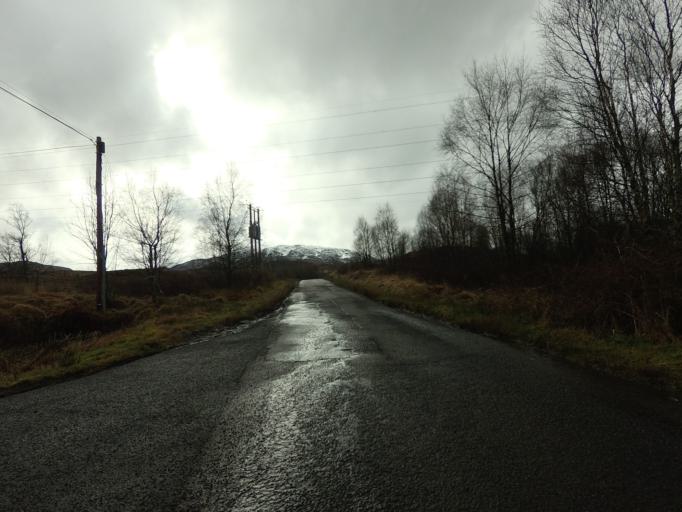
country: GB
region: Scotland
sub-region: West Dunbartonshire
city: Balloch
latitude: 56.2559
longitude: -4.5839
